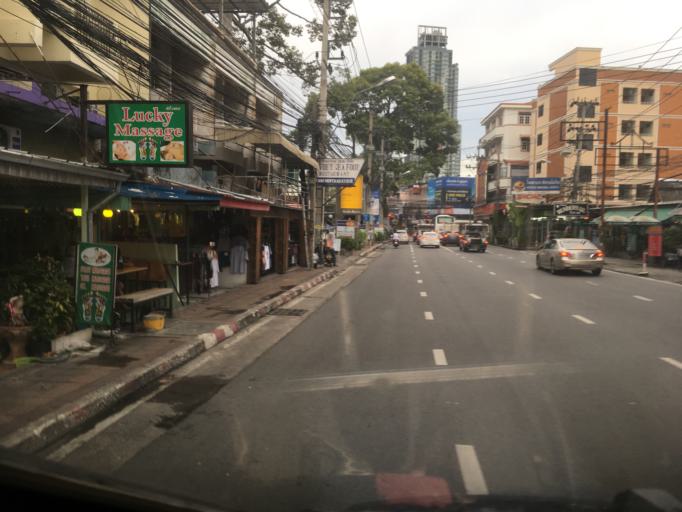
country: TH
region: Chon Buri
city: Phatthaya
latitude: 12.9358
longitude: 100.8860
